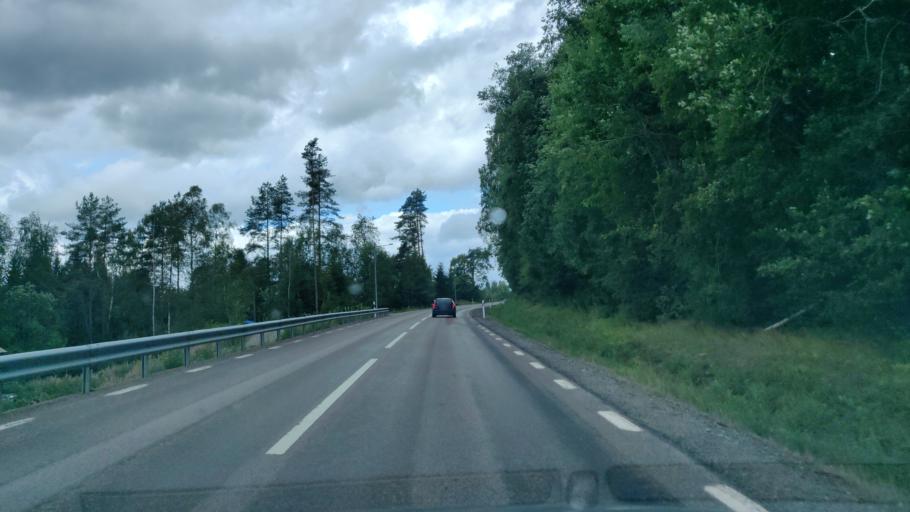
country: SE
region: Vaermland
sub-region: Torsby Kommun
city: Torsby
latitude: 60.5995
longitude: 13.0661
